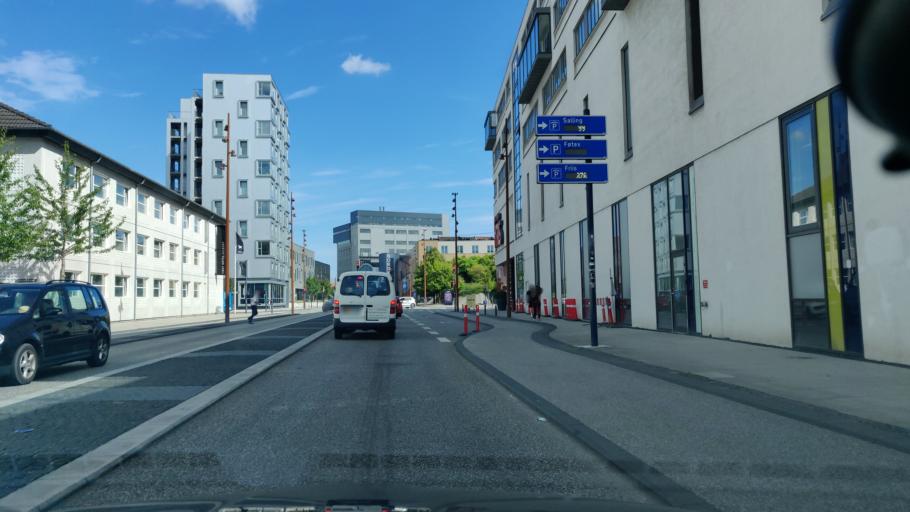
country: DK
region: North Denmark
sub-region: Alborg Kommune
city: Aalborg
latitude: 57.0483
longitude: 9.9267
